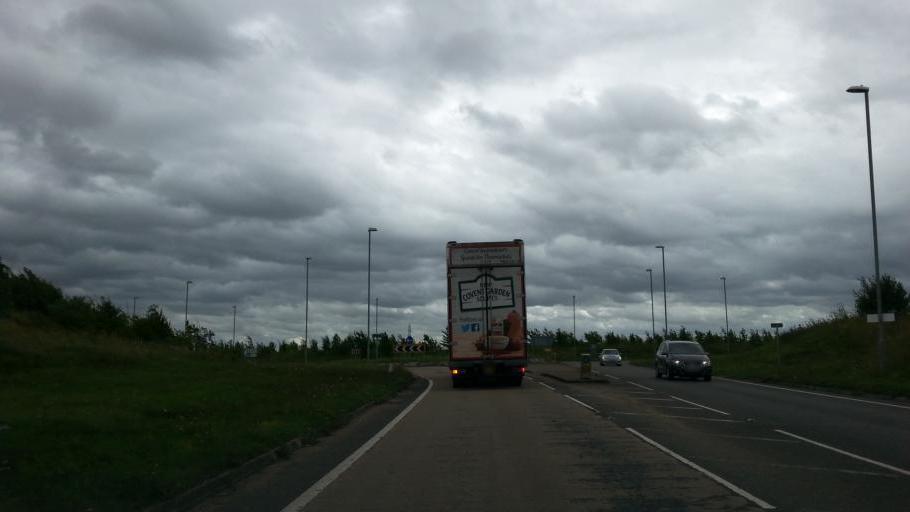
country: GB
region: England
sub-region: Cambridgeshire
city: Papworth Everard
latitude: 52.2451
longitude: -0.1294
